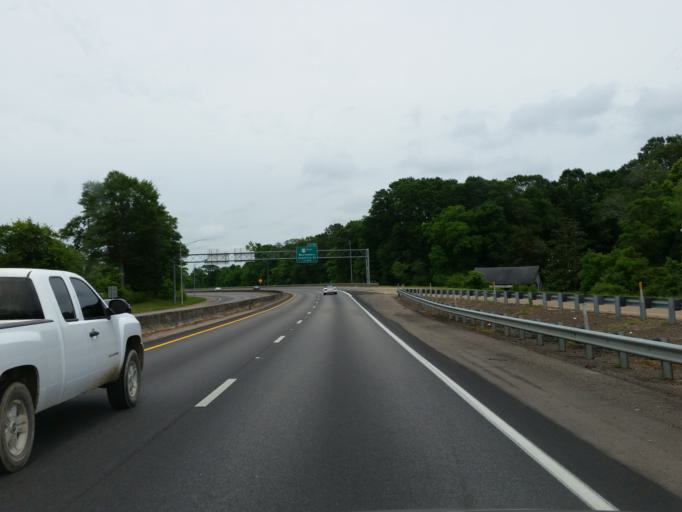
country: US
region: Mississippi
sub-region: Jones County
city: Laurel
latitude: 31.6883
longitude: -89.1213
